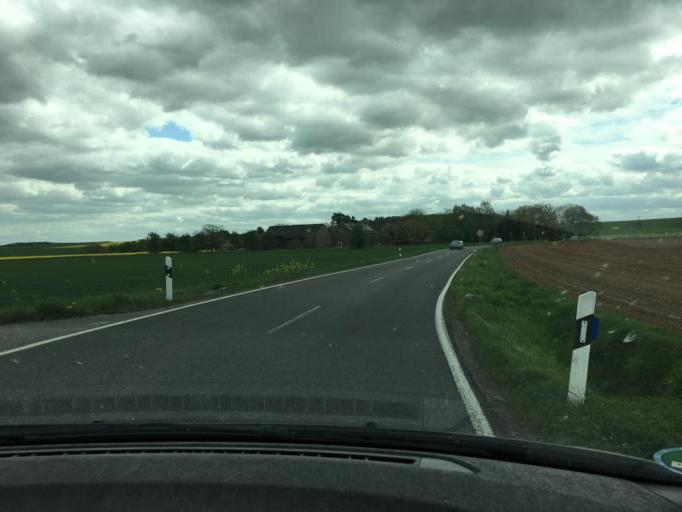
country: DE
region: North Rhine-Westphalia
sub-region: Regierungsbezirk Koln
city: Mechernich
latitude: 50.6408
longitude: 6.6642
